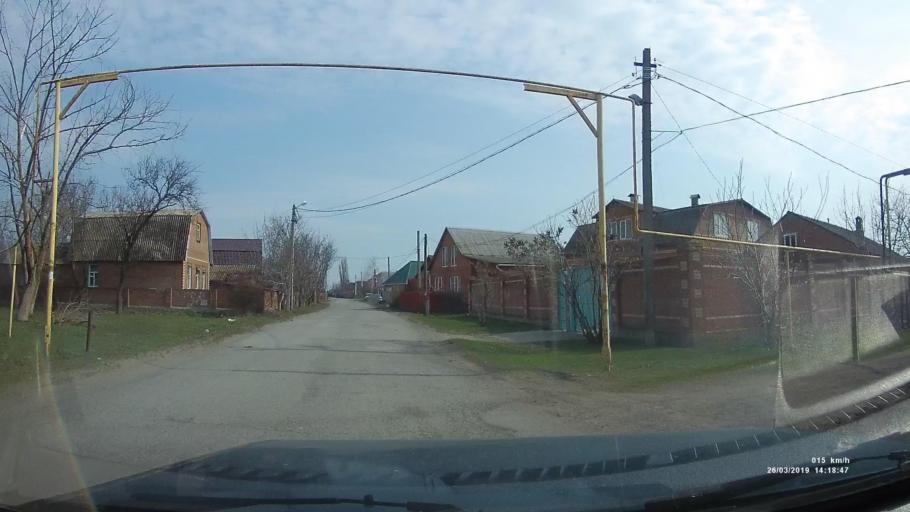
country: RU
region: Rostov
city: Novobessergenovka
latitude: 47.1903
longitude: 38.8664
